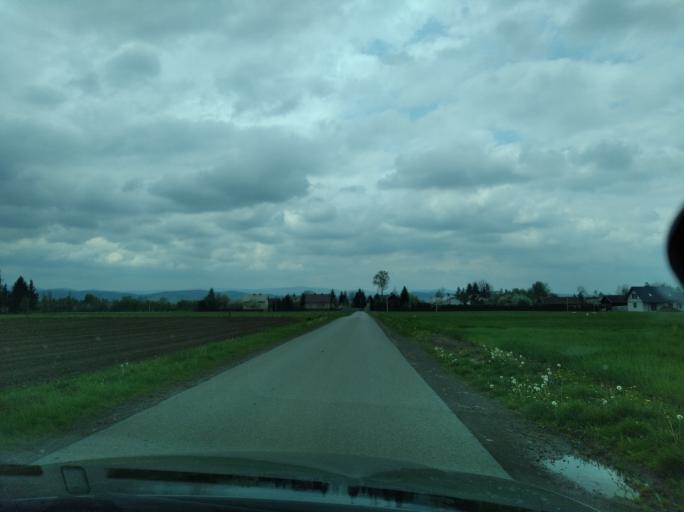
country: PL
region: Subcarpathian Voivodeship
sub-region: Powiat sanocki
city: Zarszyn
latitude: 49.6207
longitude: 22.0096
